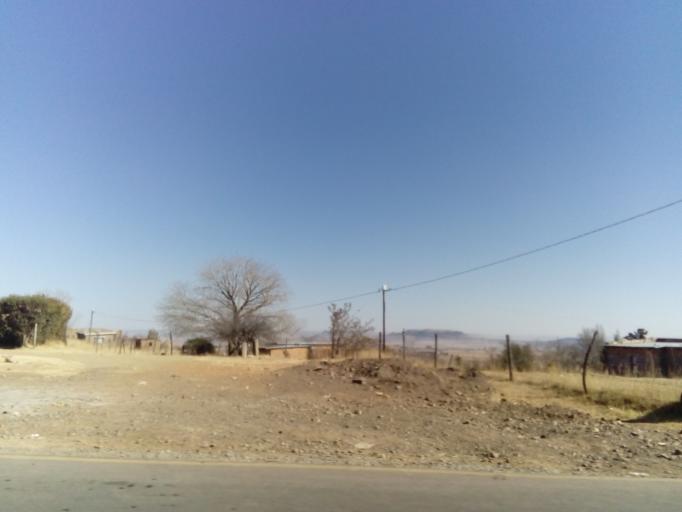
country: LS
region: Berea
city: Teyateyaneng
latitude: -29.1172
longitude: 27.8230
